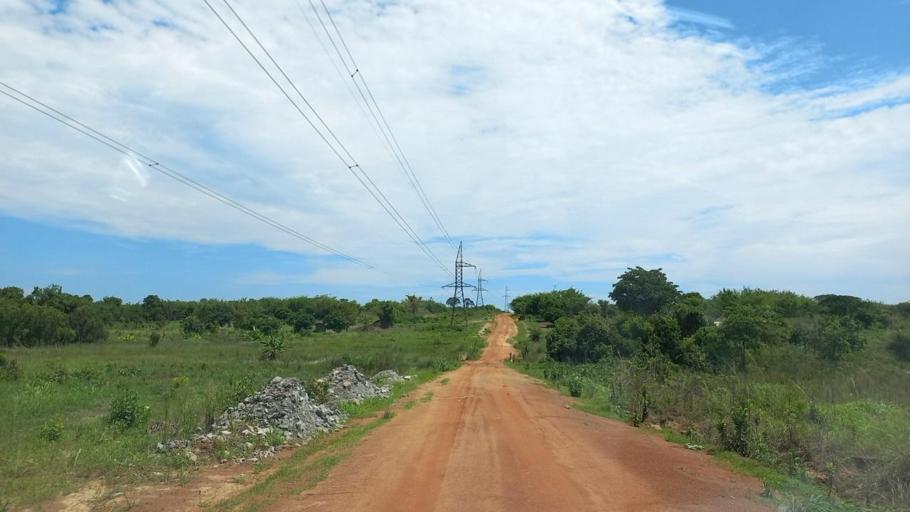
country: ZM
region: Copperbelt
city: Kitwe
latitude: -12.8299
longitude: 28.3465
